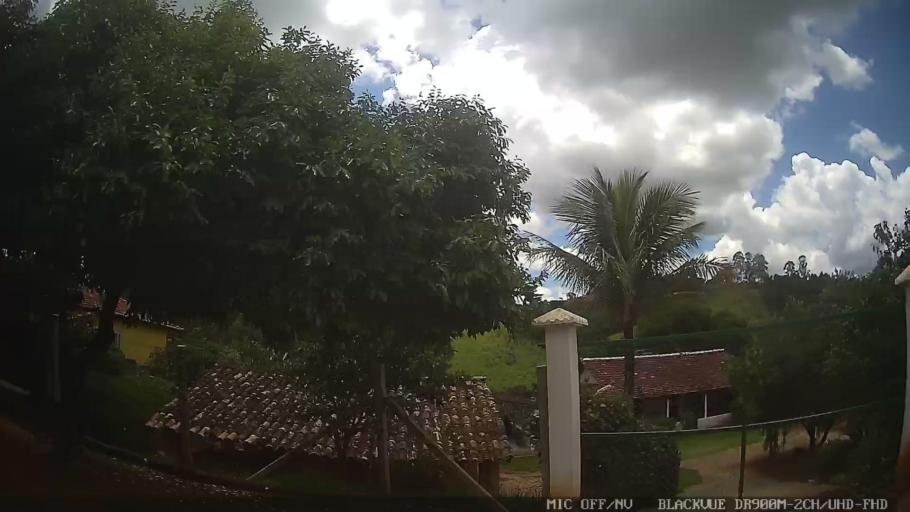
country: BR
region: Sao Paulo
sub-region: Braganca Paulista
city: Braganca Paulista
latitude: -23.0185
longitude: -46.5004
